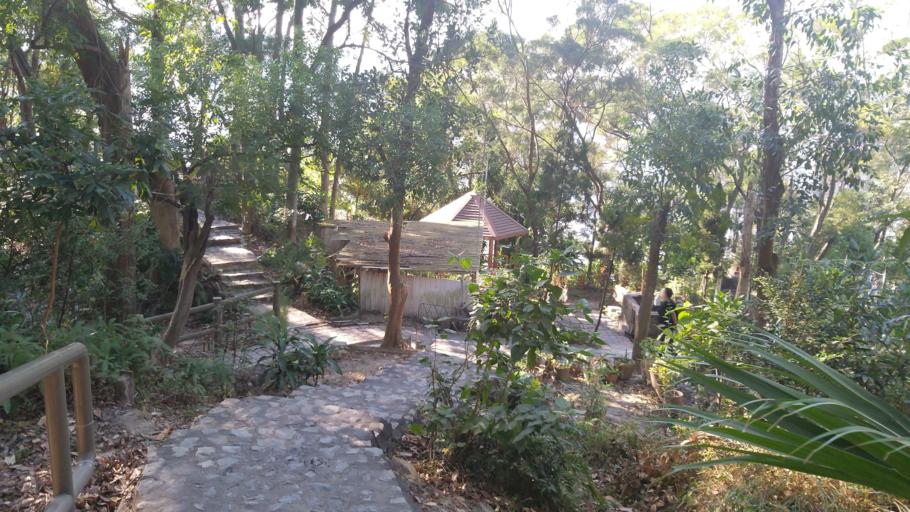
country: HK
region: Tuen Mun
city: Tuen Mun
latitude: 22.4001
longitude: 113.9839
